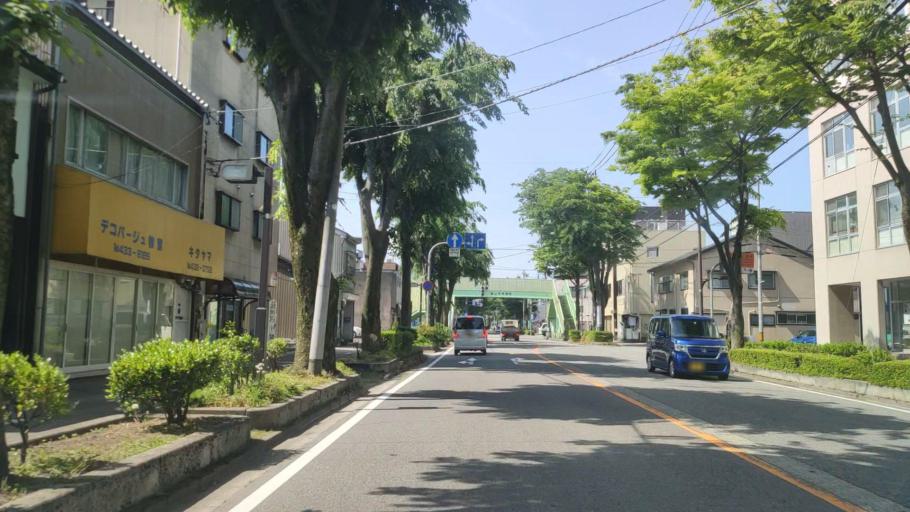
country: JP
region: Toyama
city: Toyama-shi
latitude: 36.7010
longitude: 137.2072
